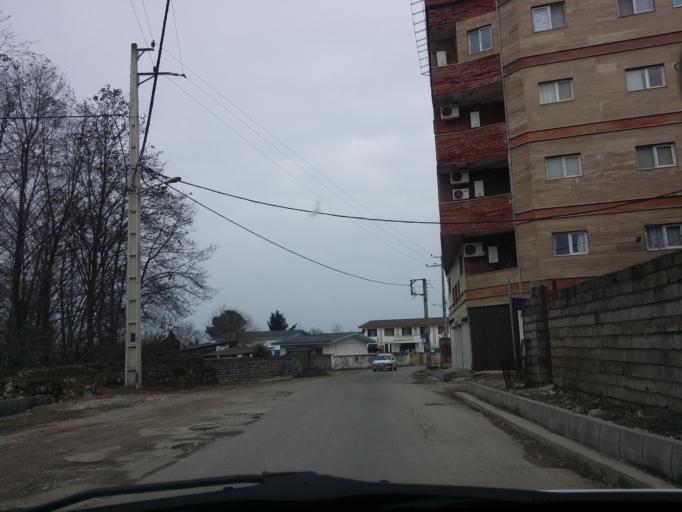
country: IR
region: Mazandaran
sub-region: Nowshahr
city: Nowshahr
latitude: 36.6427
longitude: 51.4801
